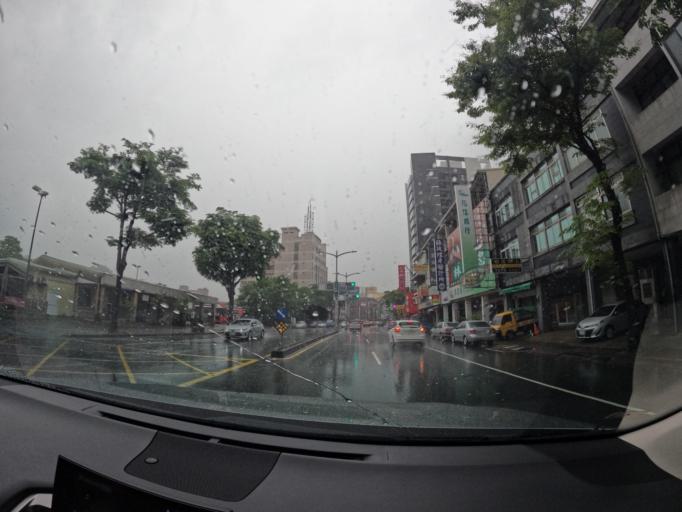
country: TW
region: Kaohsiung
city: Kaohsiung
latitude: 22.6654
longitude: 120.3219
